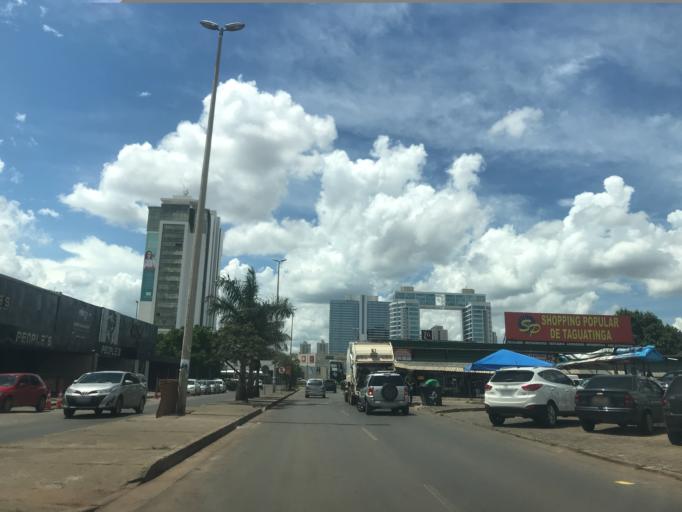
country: BR
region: Federal District
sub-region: Brasilia
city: Brasilia
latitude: -15.8458
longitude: -48.0427
